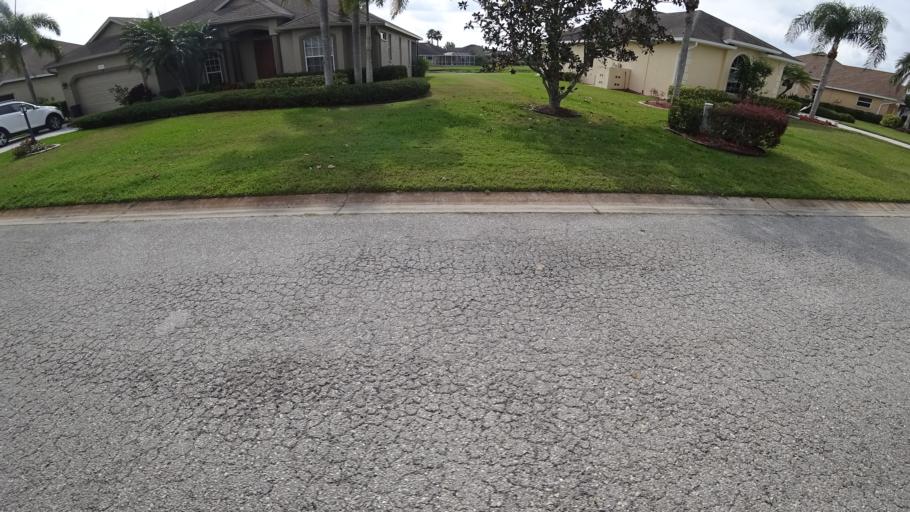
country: US
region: Florida
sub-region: Manatee County
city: Ellenton
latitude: 27.5699
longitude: -82.4736
